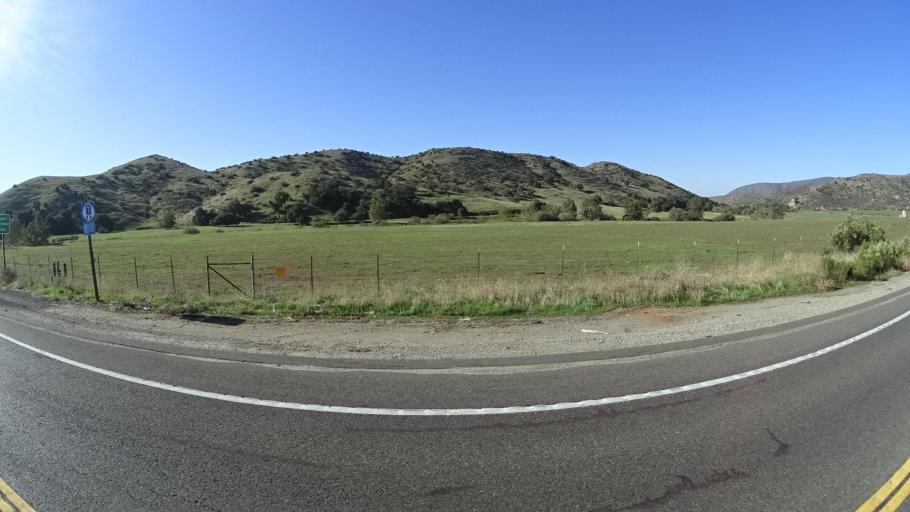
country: US
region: California
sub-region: San Diego County
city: Jamul
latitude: 32.6705
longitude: -116.8259
